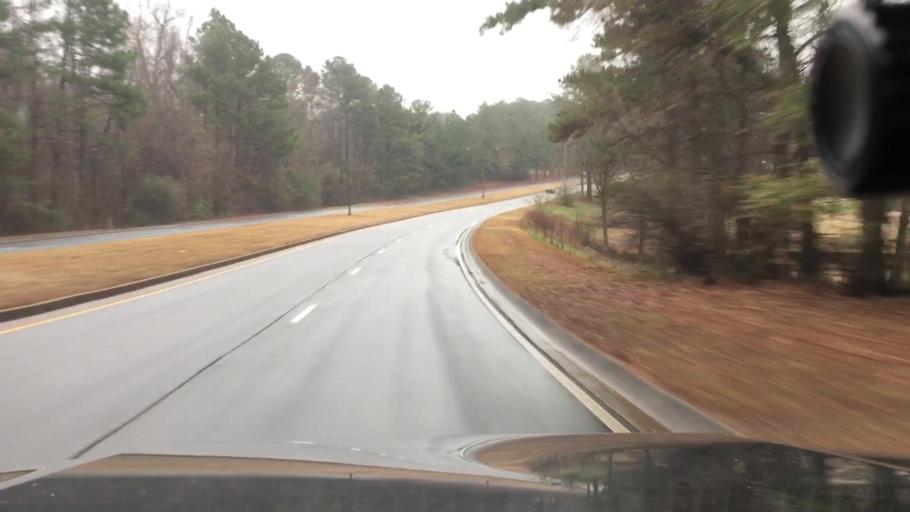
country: US
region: Georgia
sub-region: Coweta County
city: East Newnan
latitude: 33.3875
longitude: -84.7374
